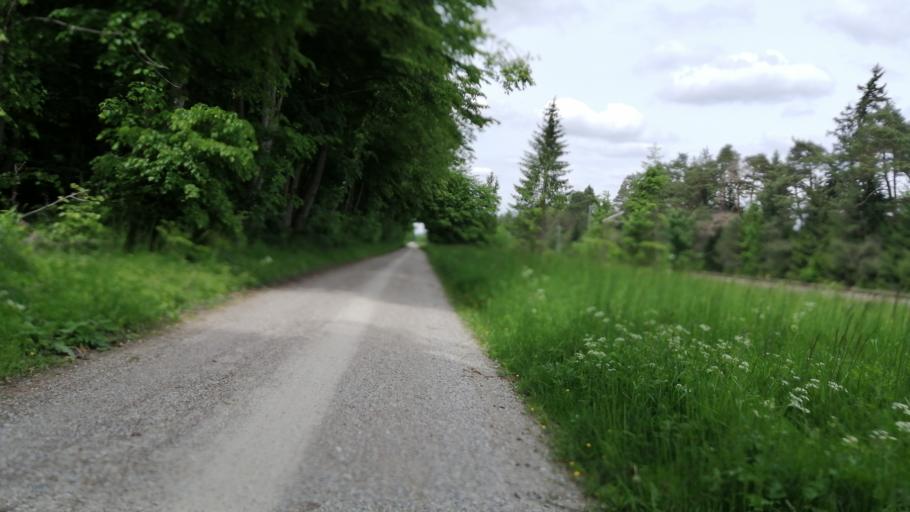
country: DE
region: Bavaria
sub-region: Upper Bavaria
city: Oberhaching
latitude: 48.0518
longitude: 11.5679
